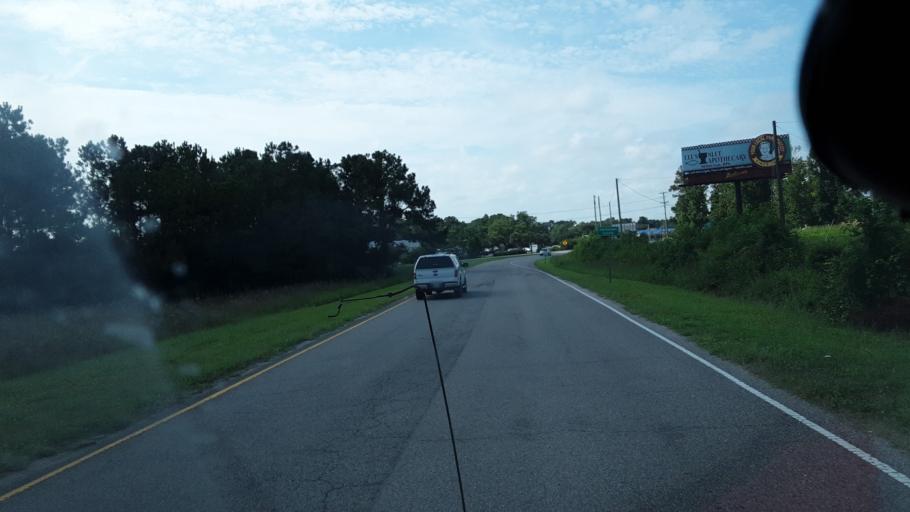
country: US
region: South Carolina
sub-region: Georgetown County
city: Murrells Inlet
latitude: 33.5717
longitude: -79.0320
